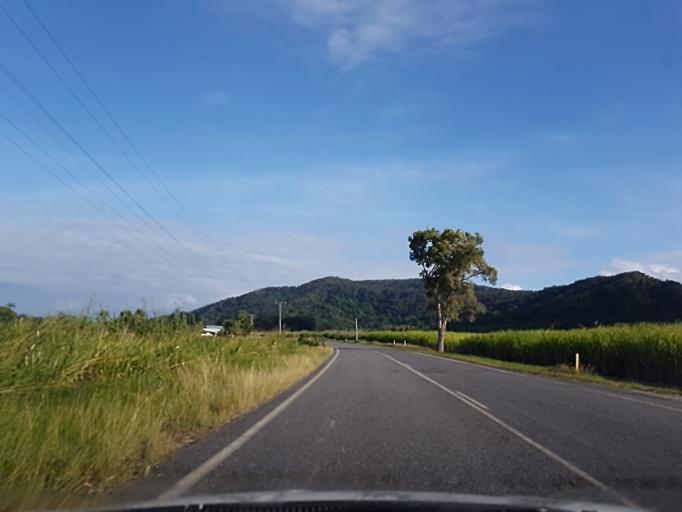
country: AU
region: Queensland
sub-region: Cairns
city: Port Douglas
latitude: -16.3414
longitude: 145.4092
